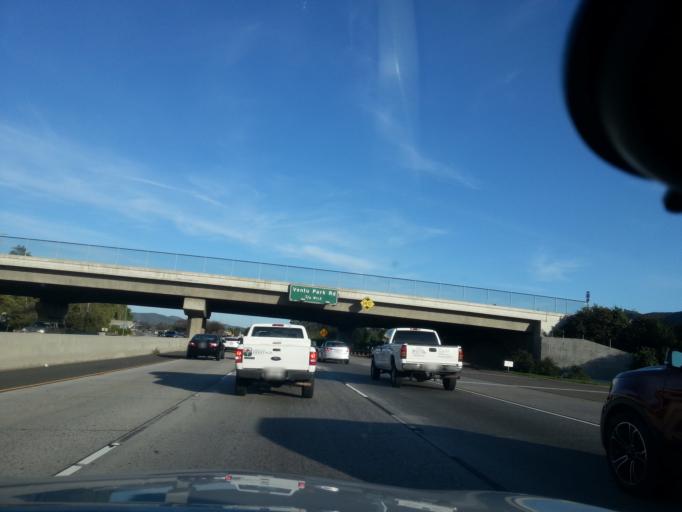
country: US
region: California
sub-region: Ventura County
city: Casa Conejo
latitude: 34.1845
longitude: -118.9266
